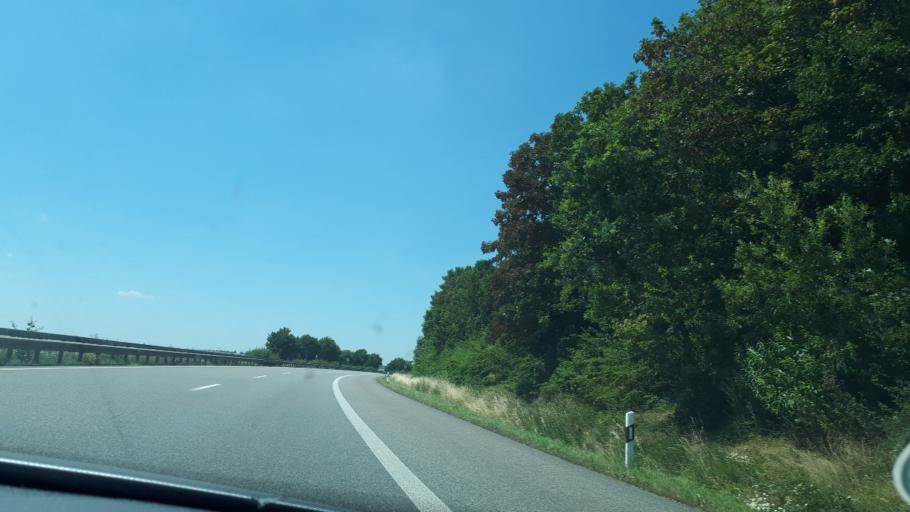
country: DE
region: Rheinland-Pfalz
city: Trimbs
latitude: 50.3028
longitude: 7.2869
